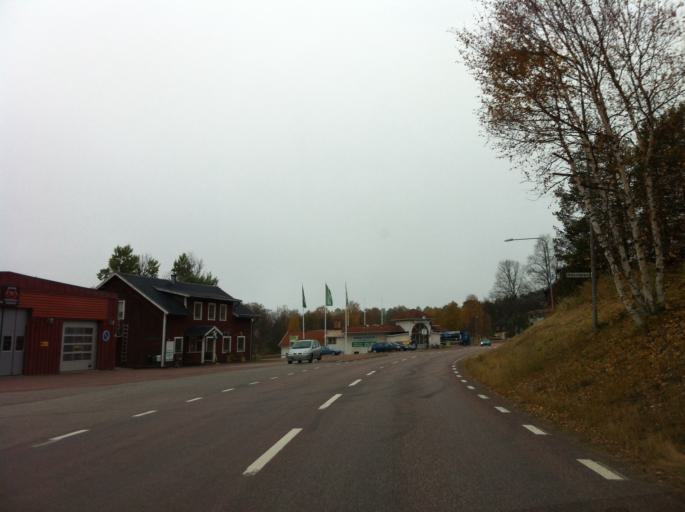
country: NO
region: Hedmark
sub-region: Trysil
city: Innbygda
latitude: 61.8572
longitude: 12.7288
